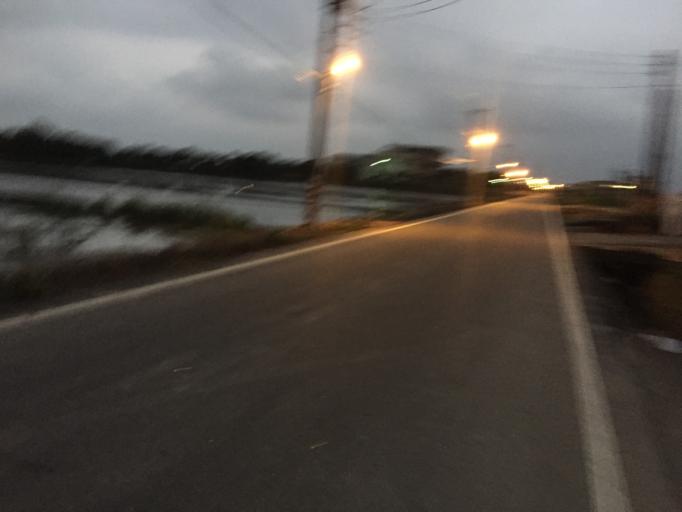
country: TW
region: Taiwan
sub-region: Yilan
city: Yilan
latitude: 24.6585
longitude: 121.7820
